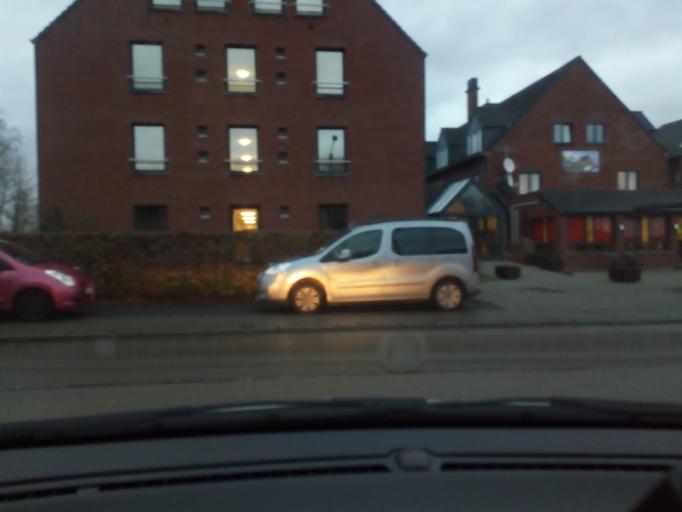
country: BE
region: Wallonia
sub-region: Province du Hainaut
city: Roeulx
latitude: 50.4666
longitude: 4.0663
